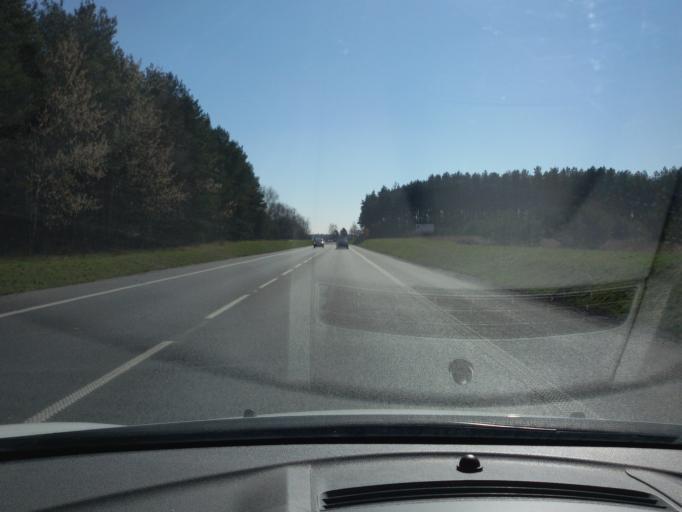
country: PL
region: Greater Poland Voivodeship
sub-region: Powiat leszczynski
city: Rydzyna
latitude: 51.7948
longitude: 16.6516
